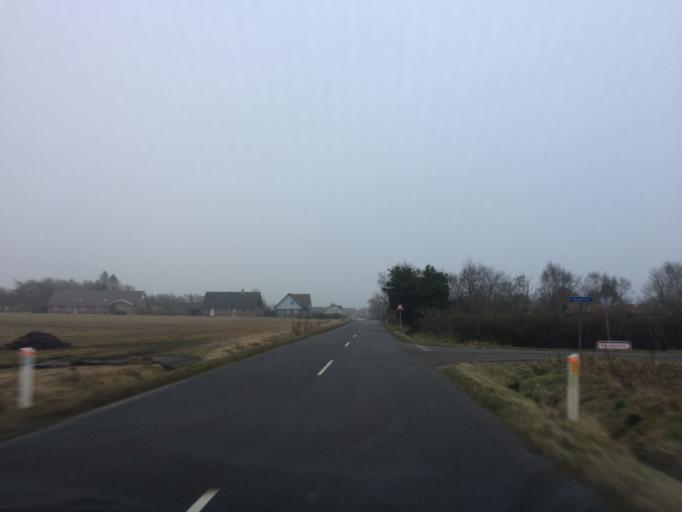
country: DK
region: South Denmark
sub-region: Varde Kommune
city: Oksbol
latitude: 55.6533
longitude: 8.3598
